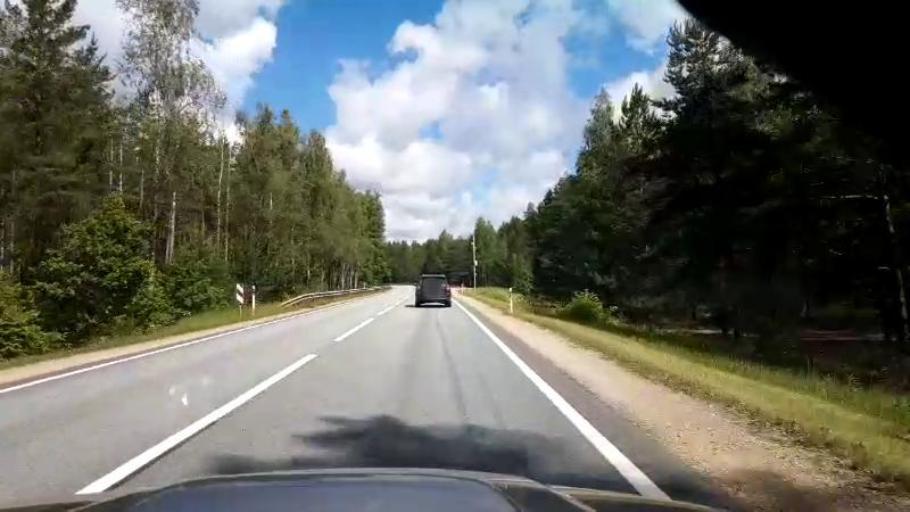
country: LV
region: Riga
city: Bergi
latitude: 56.9574
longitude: 24.3770
